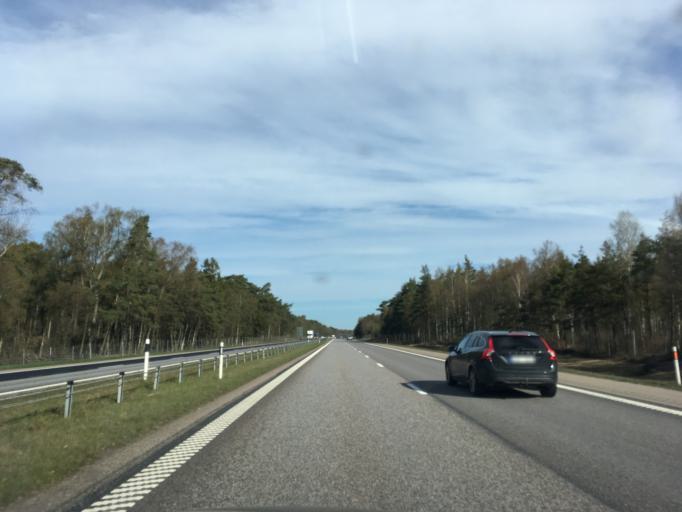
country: SE
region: Halland
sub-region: Halmstads Kommun
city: Paarp
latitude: 56.5585
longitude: 12.9578
